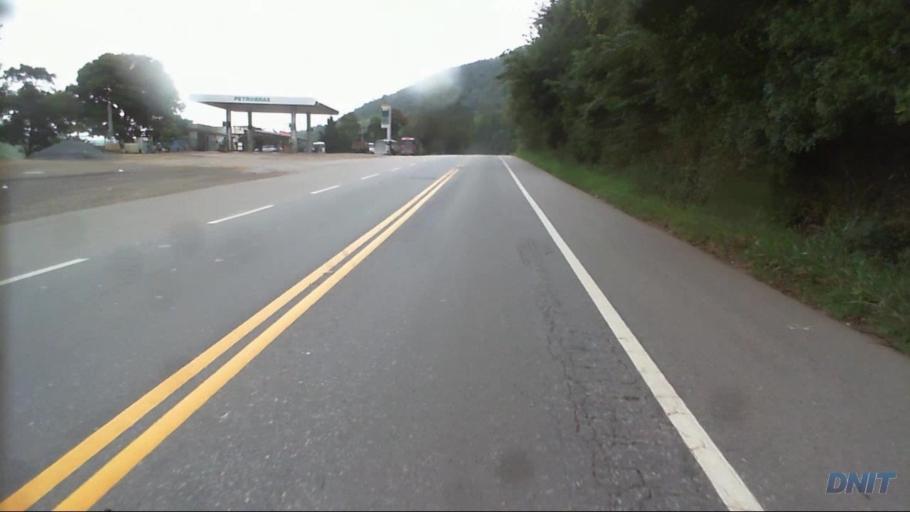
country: BR
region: Minas Gerais
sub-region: Nova Era
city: Nova Era
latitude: -19.7281
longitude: -43.0133
